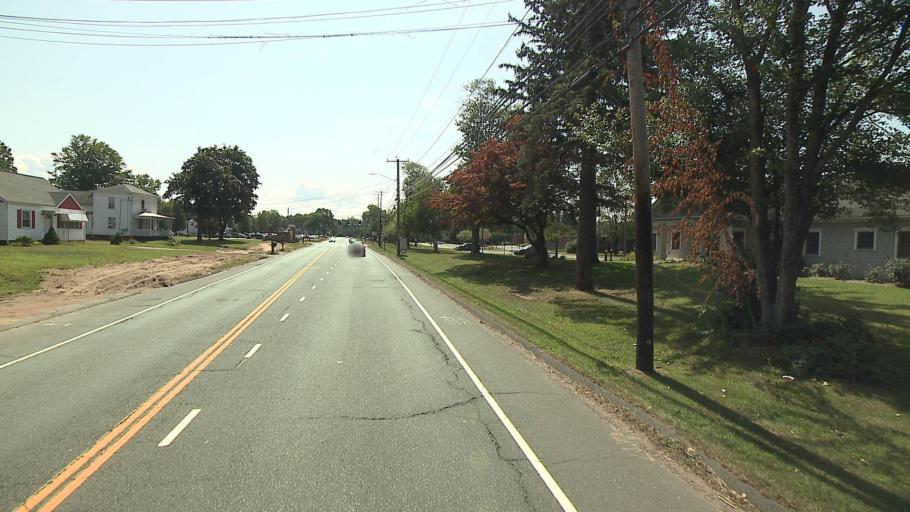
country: US
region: Connecticut
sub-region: Hartford County
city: Windsor Locks
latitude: 41.9027
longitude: -72.6118
